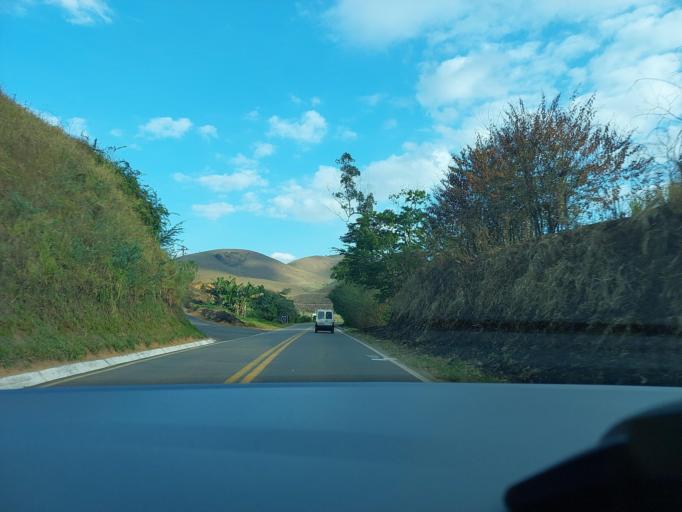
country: BR
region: Minas Gerais
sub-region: Muriae
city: Muriae
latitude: -21.0699
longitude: -42.5068
